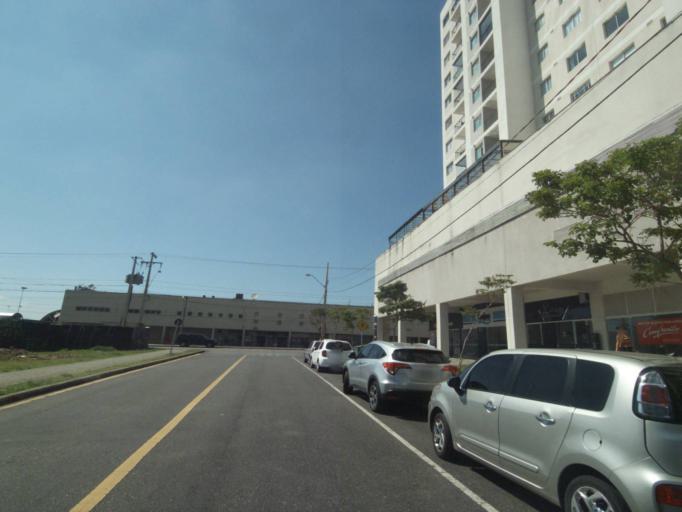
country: BR
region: Parana
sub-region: Curitiba
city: Curitiba
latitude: -25.3887
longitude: -49.2368
